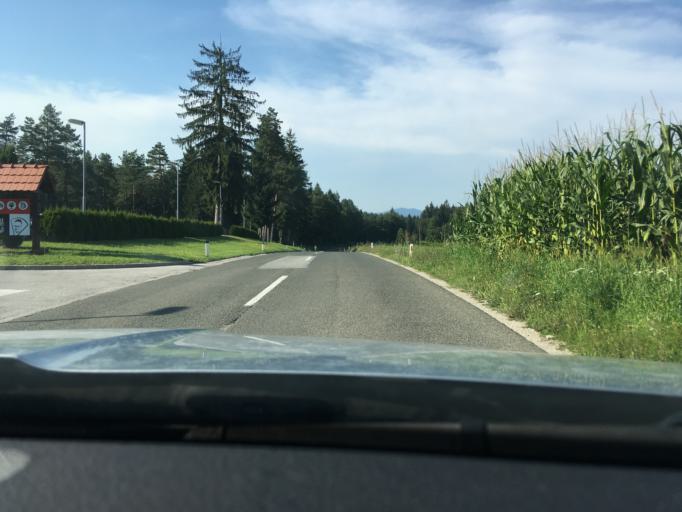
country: SI
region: Crnomelj
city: Crnomelj
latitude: 45.5468
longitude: 15.1613
